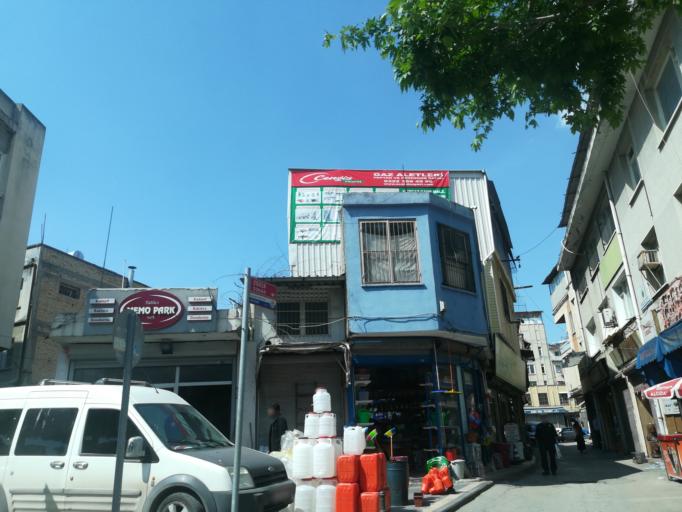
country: TR
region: Adana
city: Adana
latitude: 36.9851
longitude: 35.3318
